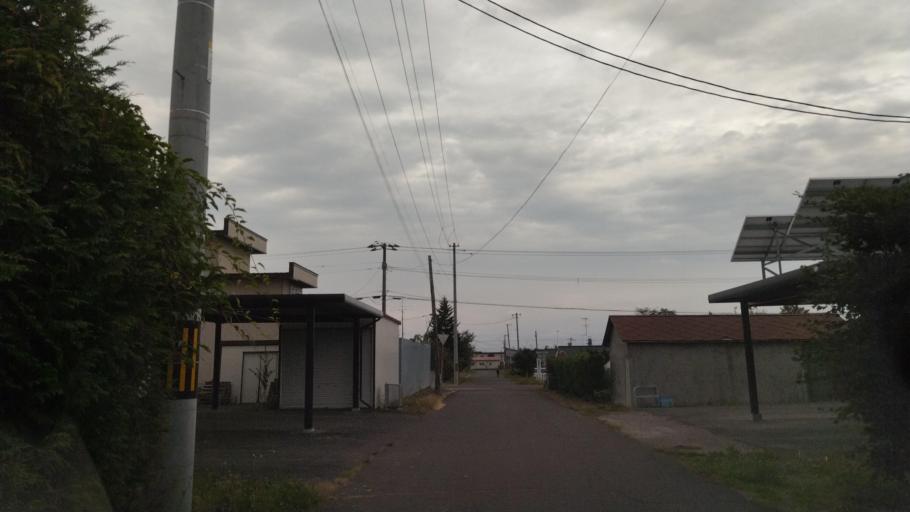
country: JP
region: Hokkaido
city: Otofuke
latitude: 43.2376
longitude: 143.2908
